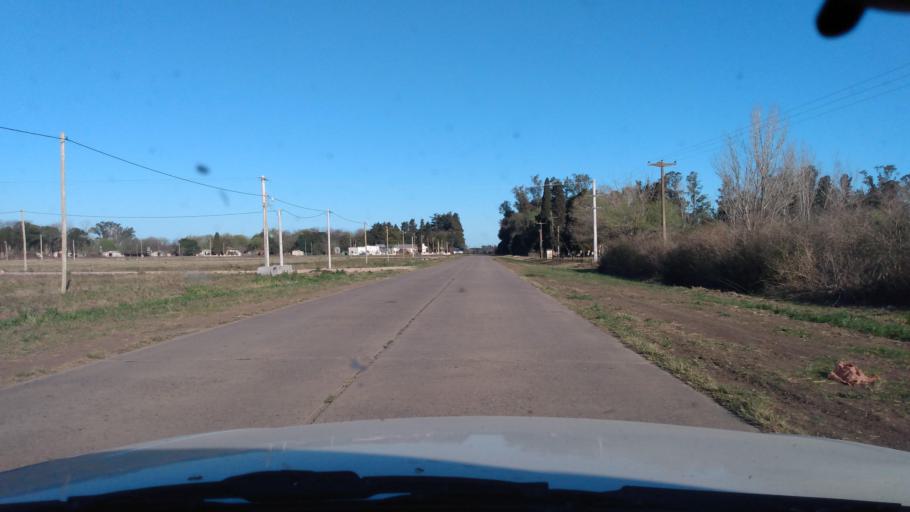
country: AR
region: Buenos Aires
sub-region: Partido de Mercedes
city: Mercedes
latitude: -34.6073
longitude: -59.2861
